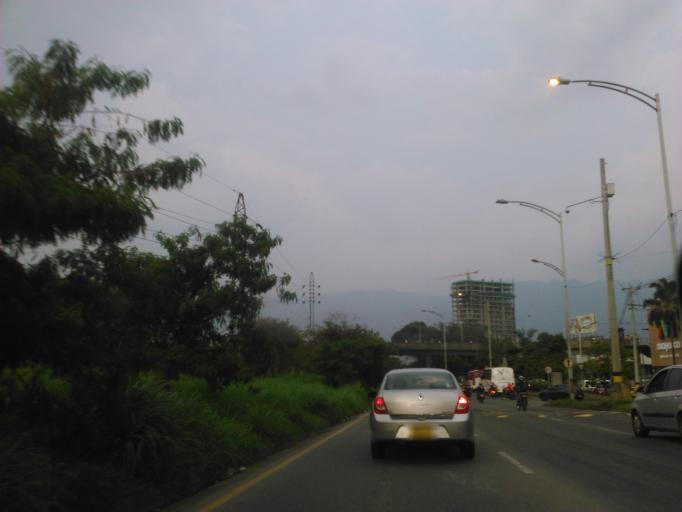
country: CO
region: Antioquia
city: Sabaneta
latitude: 6.1623
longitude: -75.6067
